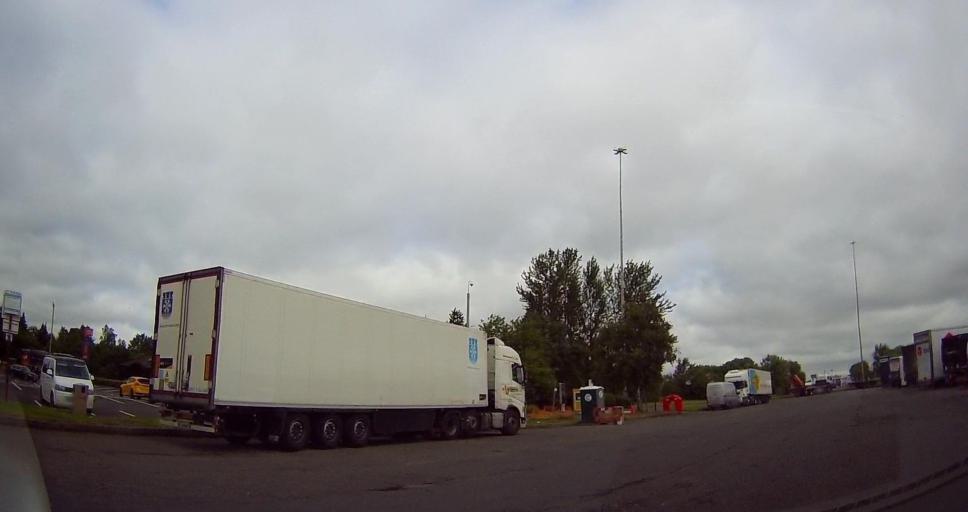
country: GB
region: Scotland
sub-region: South Lanarkshire
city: Bothwell
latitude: 55.8138
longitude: -4.0616
